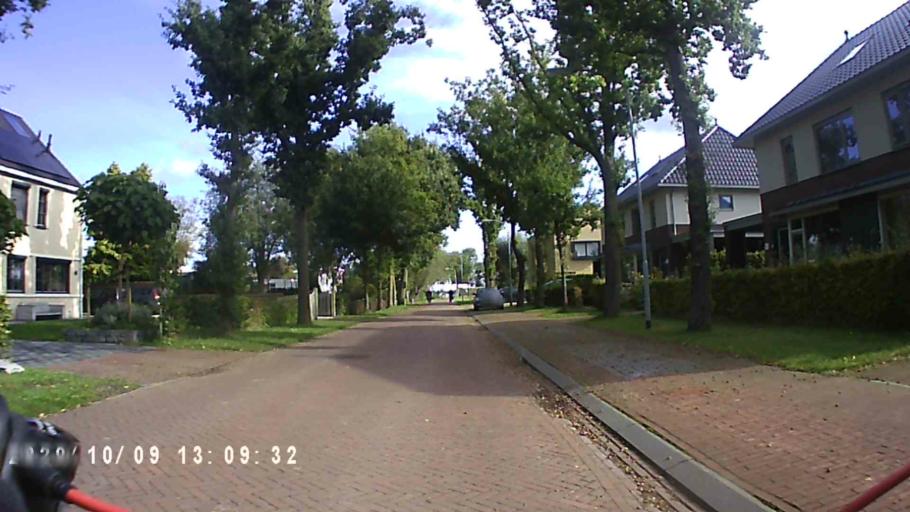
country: NL
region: Groningen
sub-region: Gemeente Zuidhorn
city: Zuidhorn
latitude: 53.2440
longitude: 6.4120
